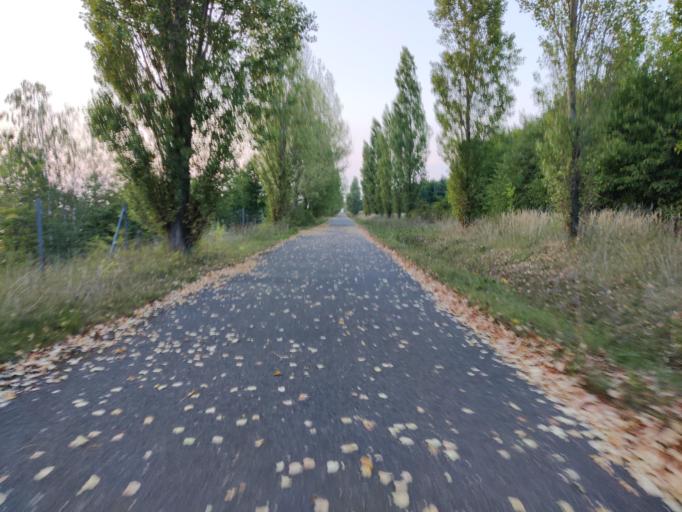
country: DE
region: Saxony
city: Zschortau
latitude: 51.4559
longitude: 12.3185
